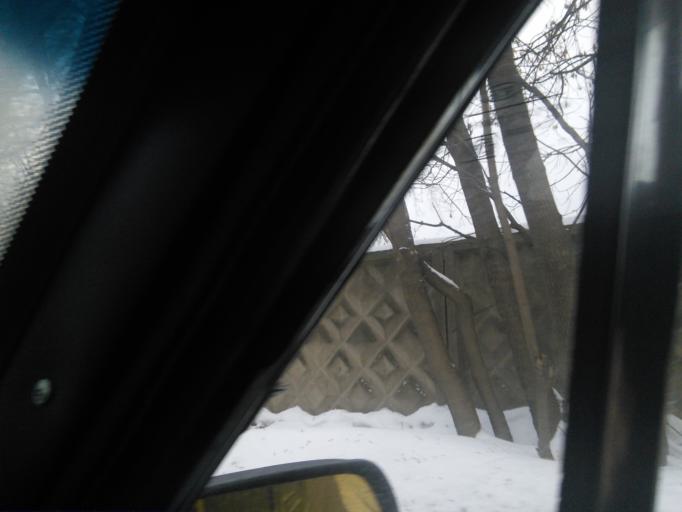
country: RU
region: Moskovskaya
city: Fili
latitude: 55.7579
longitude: 37.4720
